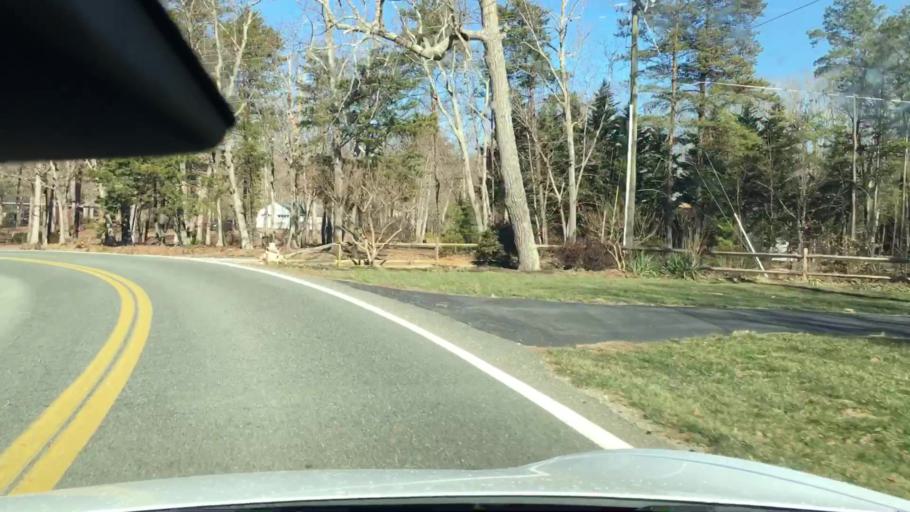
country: US
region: Virginia
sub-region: Powhatan County
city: Powhatan
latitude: 37.5559
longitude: -77.7967
